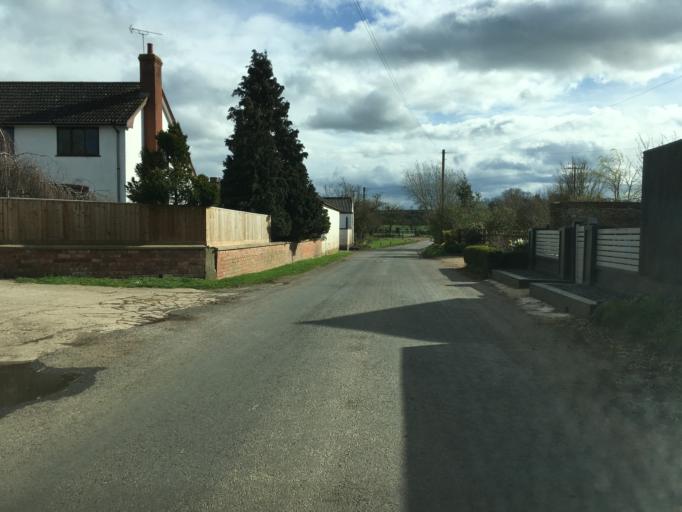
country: GB
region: England
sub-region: Gloucestershire
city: Newent
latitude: 51.8362
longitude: -2.3950
